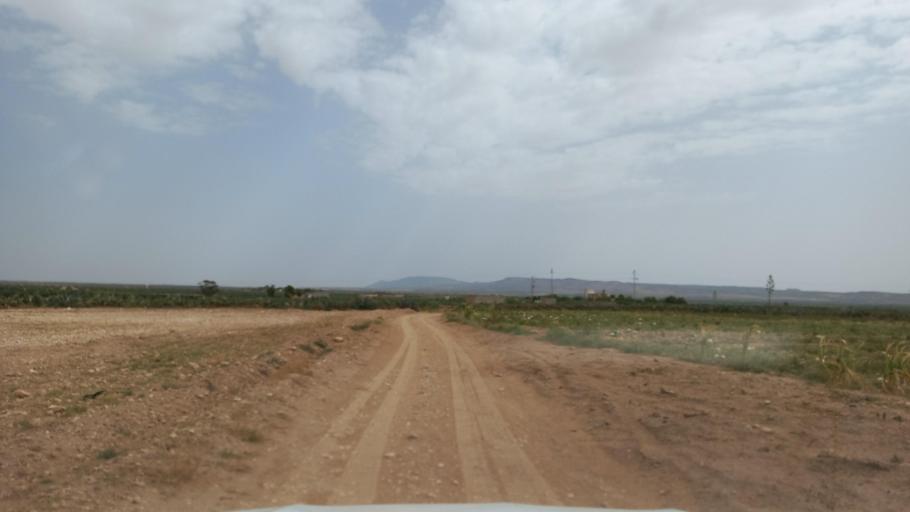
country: TN
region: Al Qasrayn
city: Kasserine
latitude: 35.2811
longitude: 9.0176
